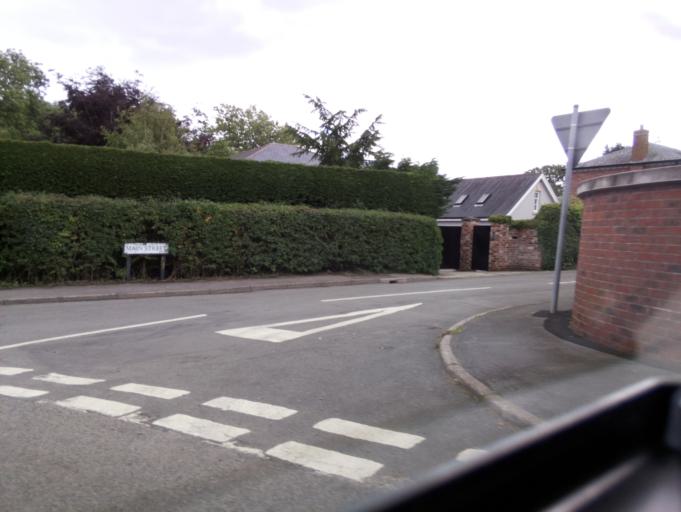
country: GB
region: England
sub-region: Nottinghamshire
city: Cotgrave
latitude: 52.8459
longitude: -1.0620
